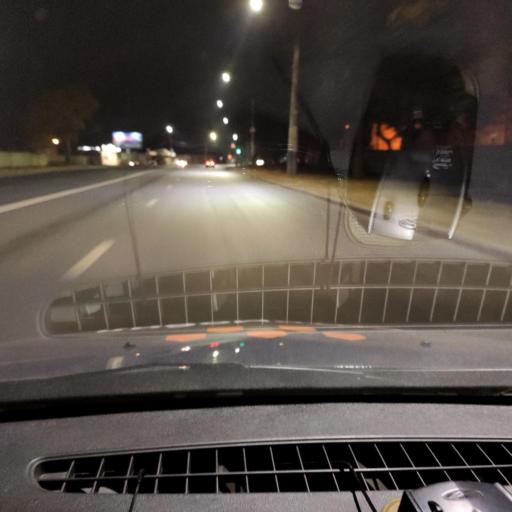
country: RU
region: Voronezj
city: Somovo
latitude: 51.7096
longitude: 39.2763
